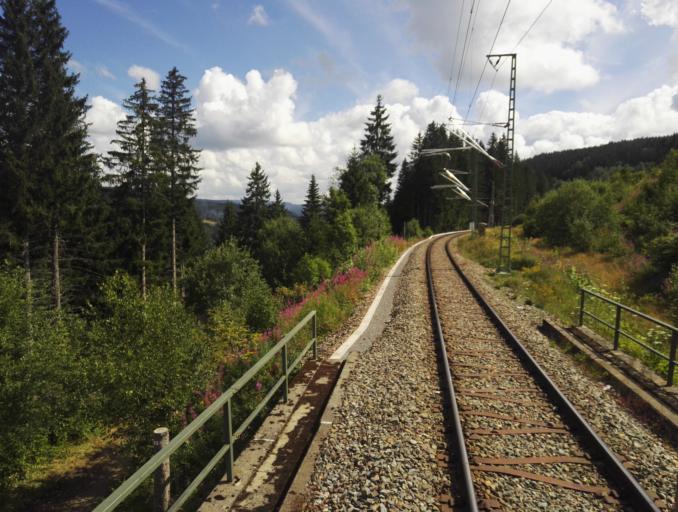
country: DE
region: Baden-Wuerttemberg
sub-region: Freiburg Region
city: Hinterzarten
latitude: 47.8736
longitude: 8.1024
